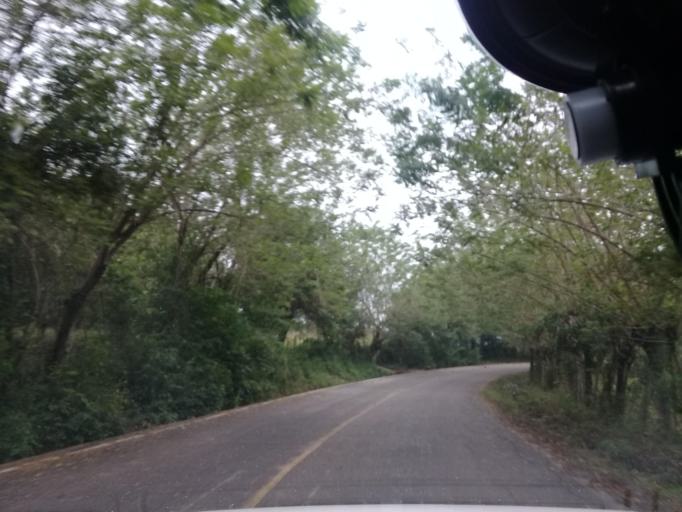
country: MX
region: Veracruz
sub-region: Chalma
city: San Pedro Coyutla
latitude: 21.2129
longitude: -98.4251
